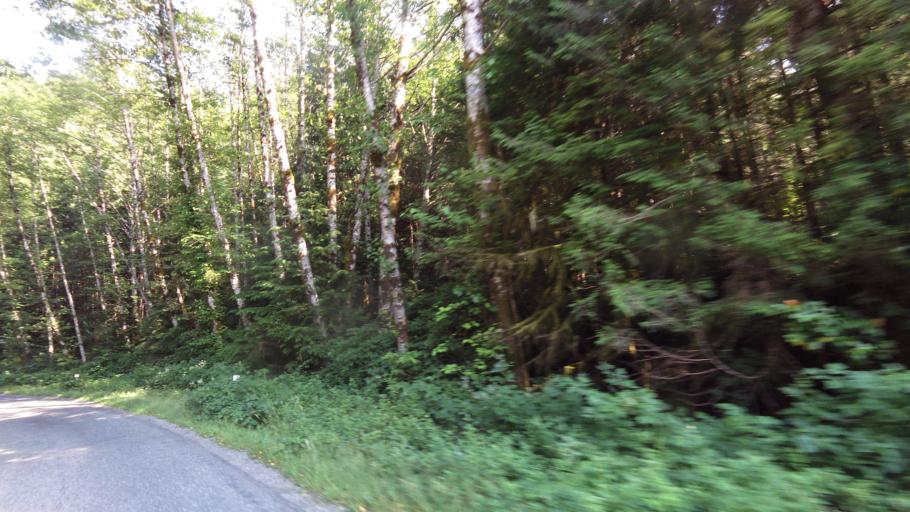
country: CA
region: British Columbia
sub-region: Regional District of Alberni-Clayoquot
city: Ucluelet
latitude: 49.0823
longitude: -125.4586
